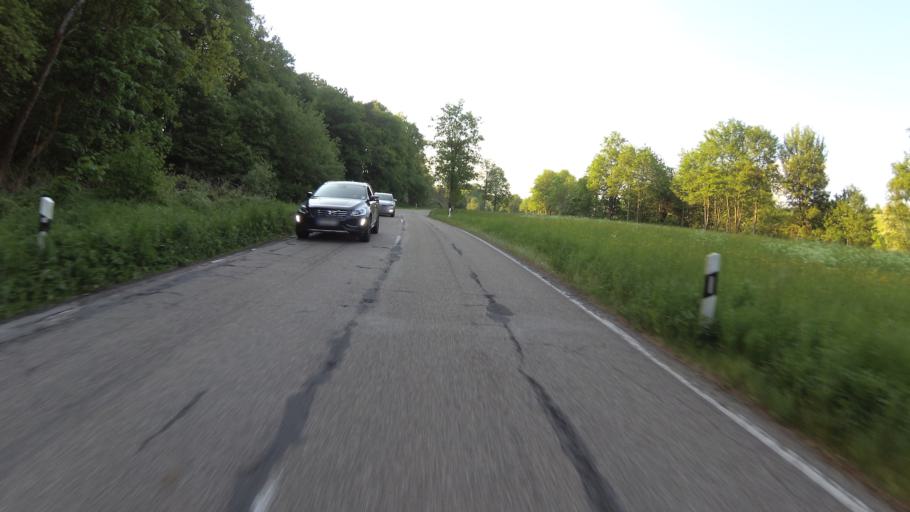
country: DE
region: Rheinland-Pfalz
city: Contwig
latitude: 49.2198
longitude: 7.4184
